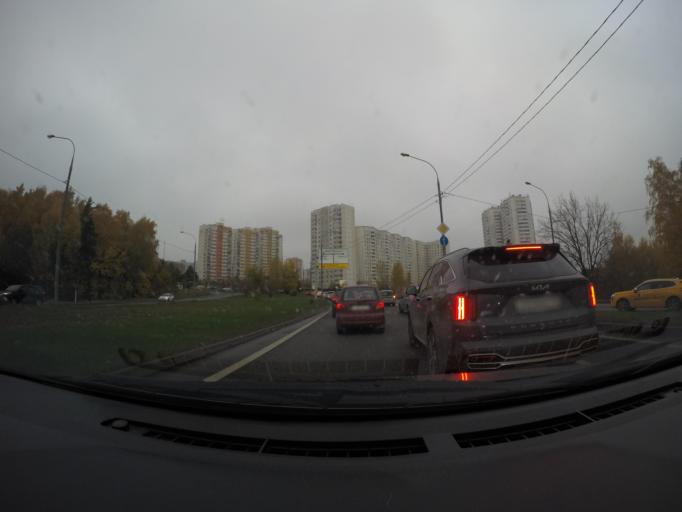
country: RU
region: Moscow
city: Annino
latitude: 55.5581
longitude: 37.5861
